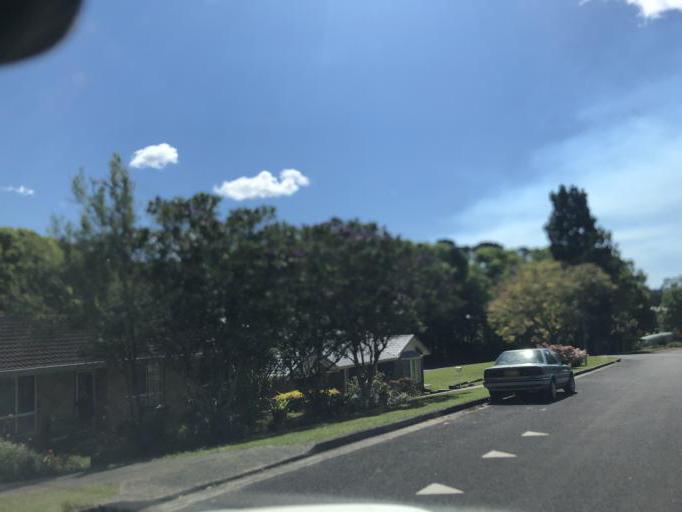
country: AU
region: New South Wales
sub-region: Bellingen
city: Bellingen
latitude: -30.4577
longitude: 152.9062
